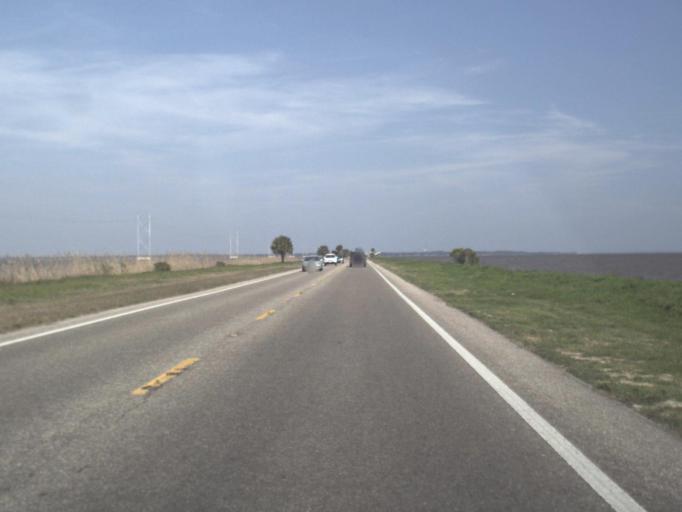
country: US
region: Florida
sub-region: Franklin County
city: Apalachicola
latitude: 29.7269
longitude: -84.9648
